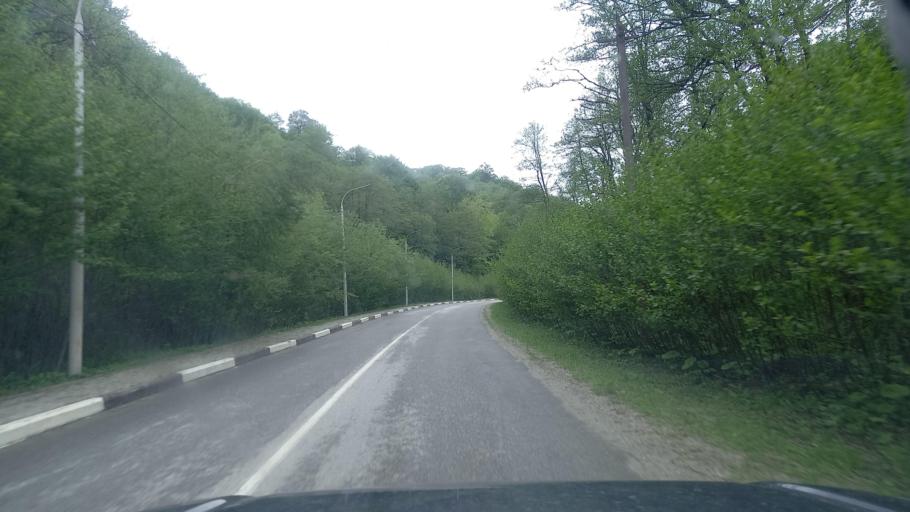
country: RU
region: Kabardino-Balkariya
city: Babugent
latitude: 43.2355
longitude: 43.5436
